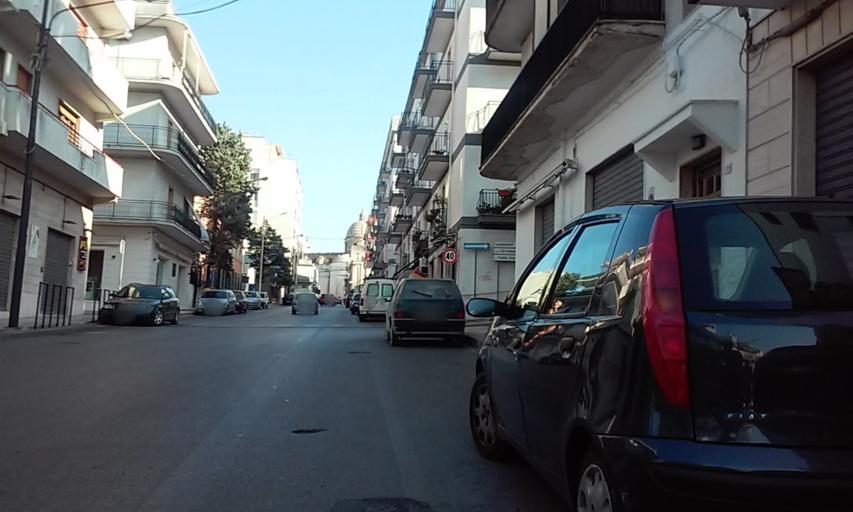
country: IT
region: Apulia
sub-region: Provincia di Brindisi
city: Ceglie Messapica
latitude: 40.6494
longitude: 17.5114
